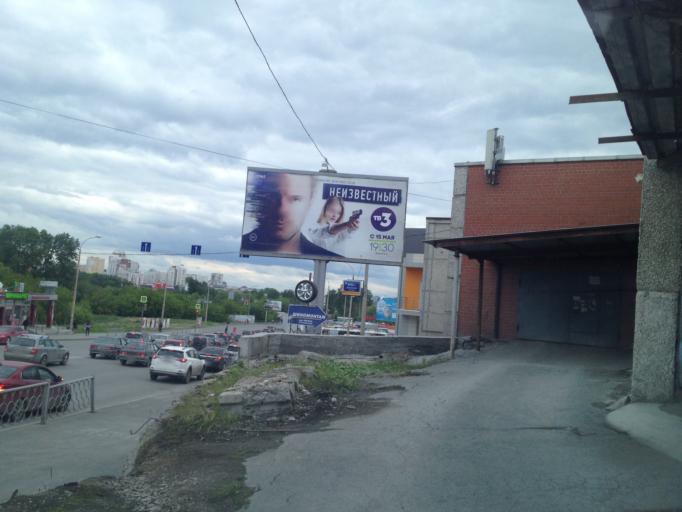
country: RU
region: Sverdlovsk
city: Yekaterinburg
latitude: 56.8493
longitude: 60.5667
